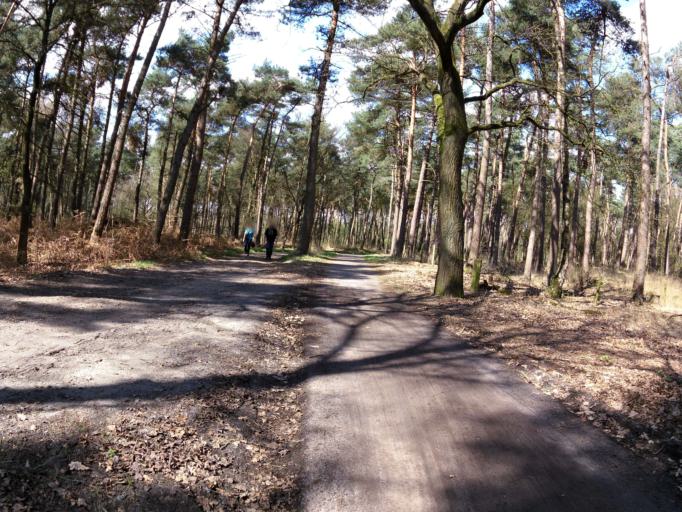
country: NL
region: North Brabant
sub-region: Gemeente Haaren
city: Haaren
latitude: 51.5788
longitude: 5.2450
